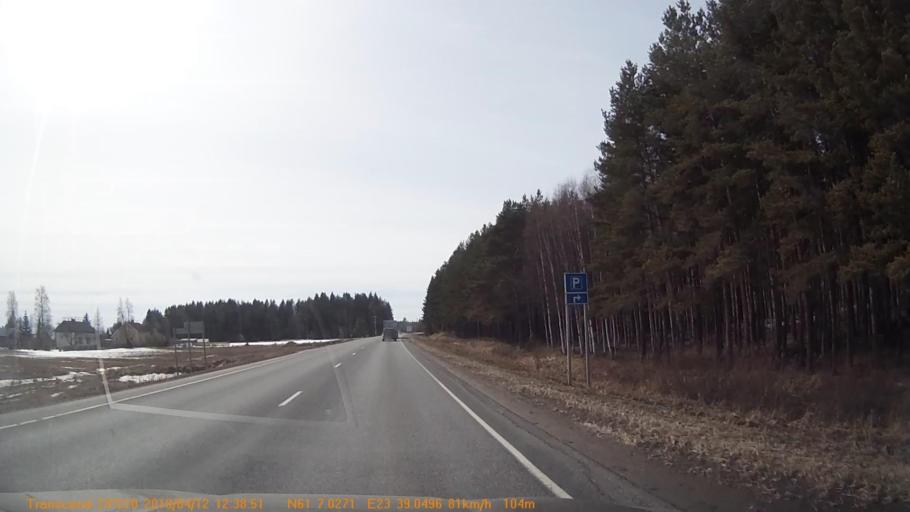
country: FI
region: Pirkanmaa
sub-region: Etelae-Pirkanmaa
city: Kylmaekoski
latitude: 61.1172
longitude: 23.6510
